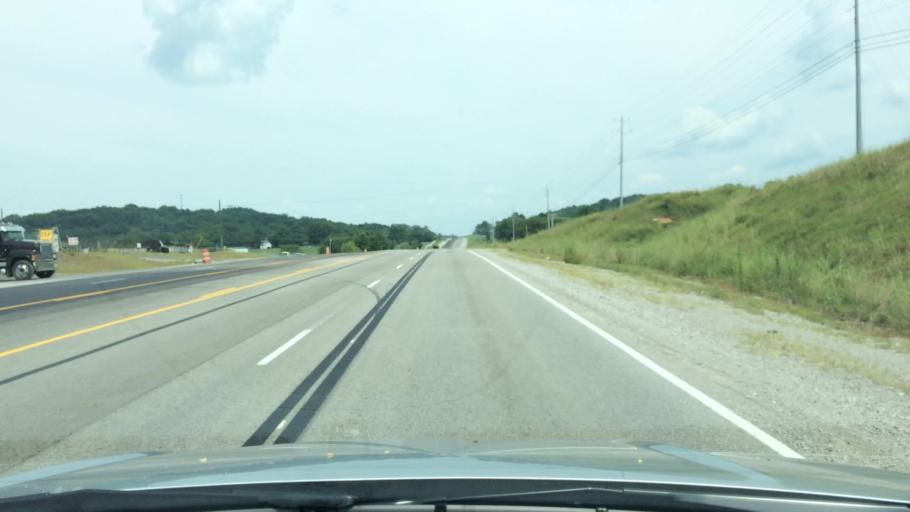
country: US
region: Tennessee
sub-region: Giles County
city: Pulaski
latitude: 35.1522
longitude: -87.0035
